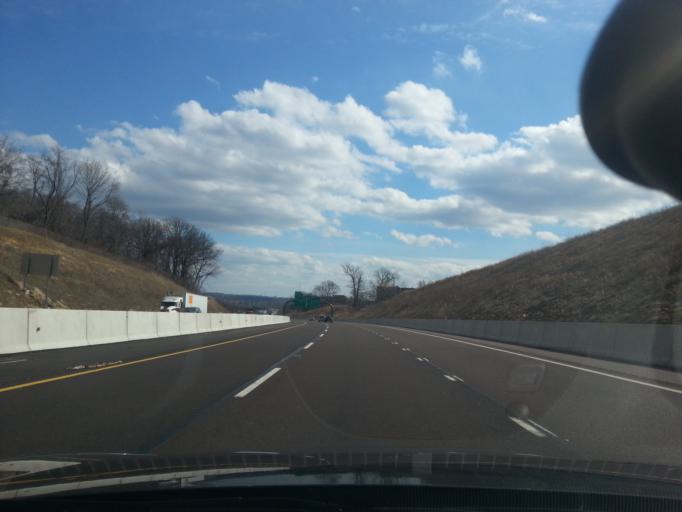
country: US
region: Pennsylvania
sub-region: Montgomery County
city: Plymouth Meeting
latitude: 40.1238
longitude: -75.2833
